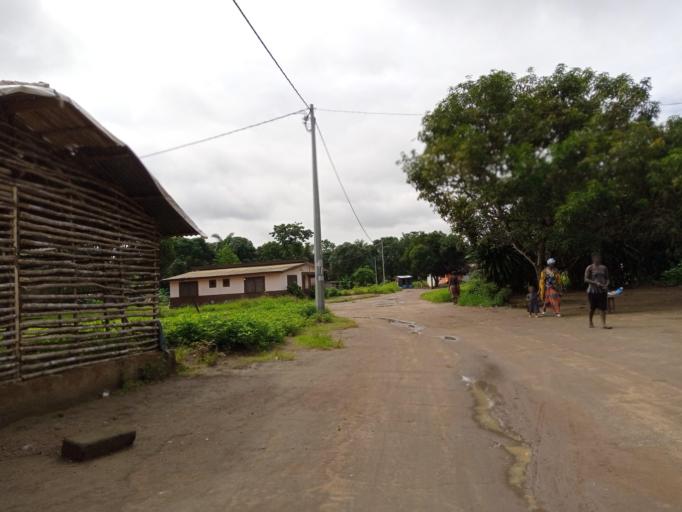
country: SL
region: Northern Province
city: Sawkta
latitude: 8.6263
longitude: -13.2046
